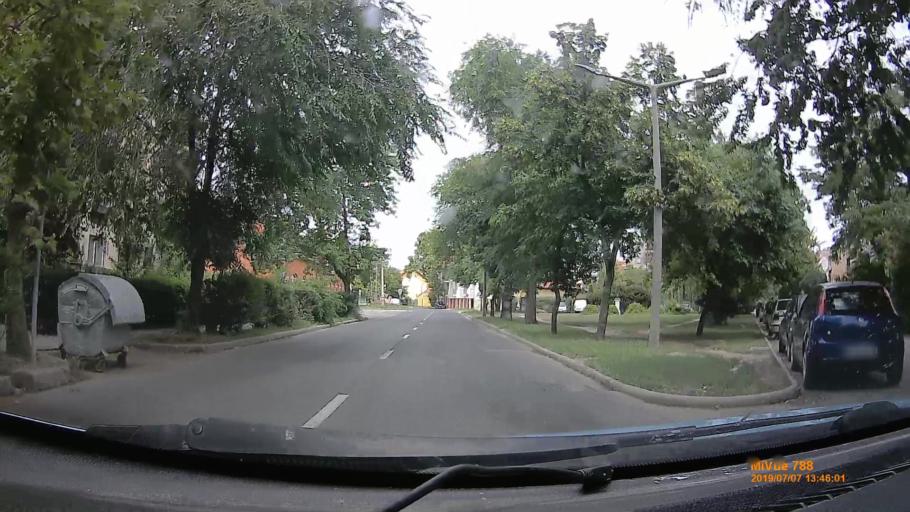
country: HU
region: Jasz-Nagykun-Szolnok
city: Szolnok
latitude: 47.1803
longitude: 20.1915
